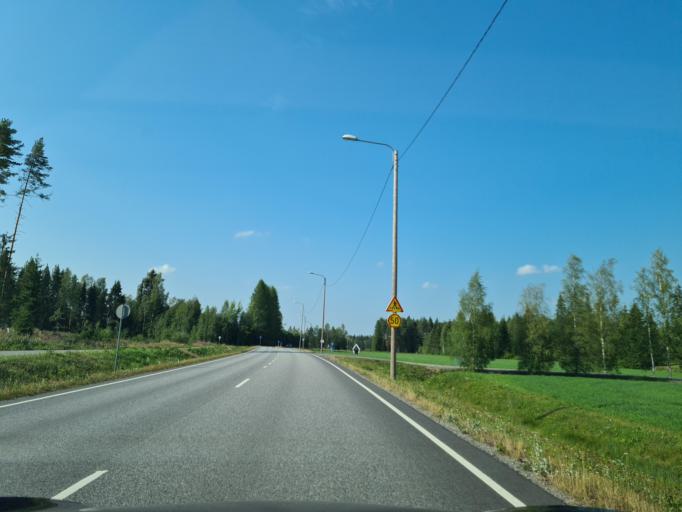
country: FI
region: Satakunta
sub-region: Pohjois-Satakunta
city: Karvia
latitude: 62.0871
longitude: 22.5271
